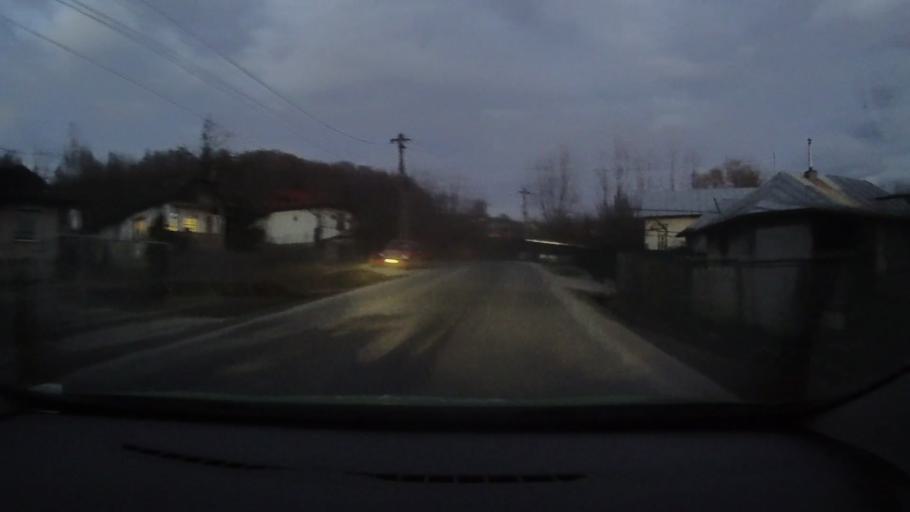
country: RO
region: Prahova
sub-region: Comuna Poiana Campina
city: Poiana Campina
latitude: 45.1287
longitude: 25.6778
